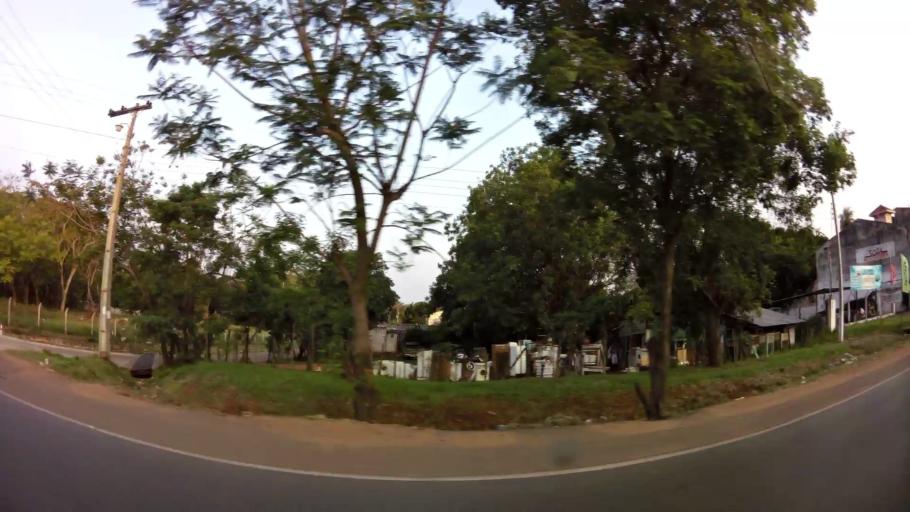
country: PY
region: Central
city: Villa Elisa
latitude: -25.3540
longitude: -57.5934
